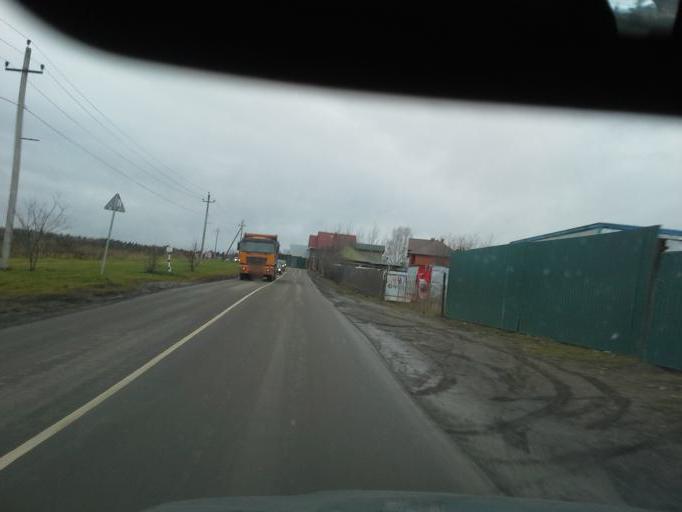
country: RU
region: Moskovskaya
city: Filimonki
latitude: 55.5717
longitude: 37.3872
